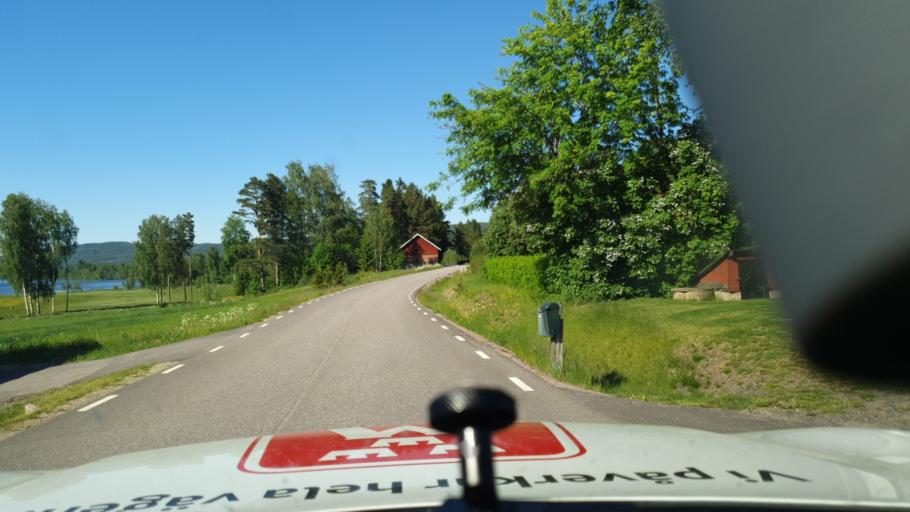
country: SE
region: Vaermland
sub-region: Torsby Kommun
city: Torsby
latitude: 60.1809
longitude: 13.0355
